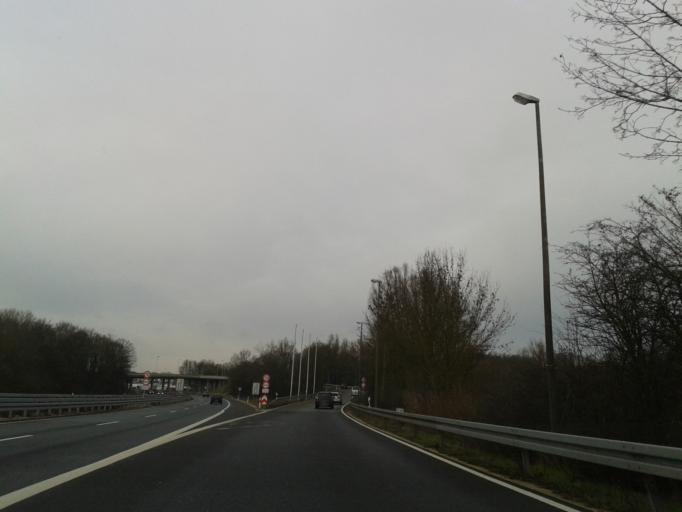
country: DE
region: Bavaria
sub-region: Upper Franconia
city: Coburg
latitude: 50.2383
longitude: 10.9738
